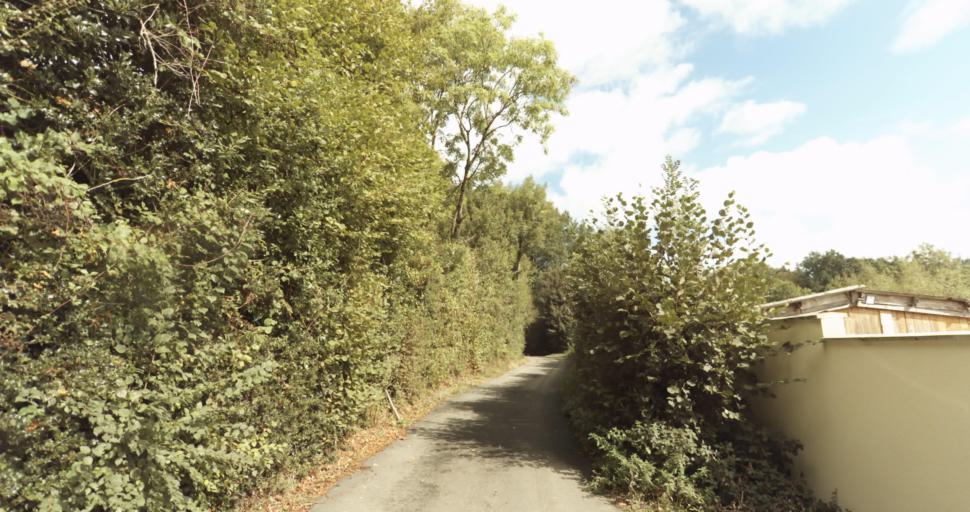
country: FR
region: Lower Normandy
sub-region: Departement de l'Orne
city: Gace
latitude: 48.8114
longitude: 0.2697
